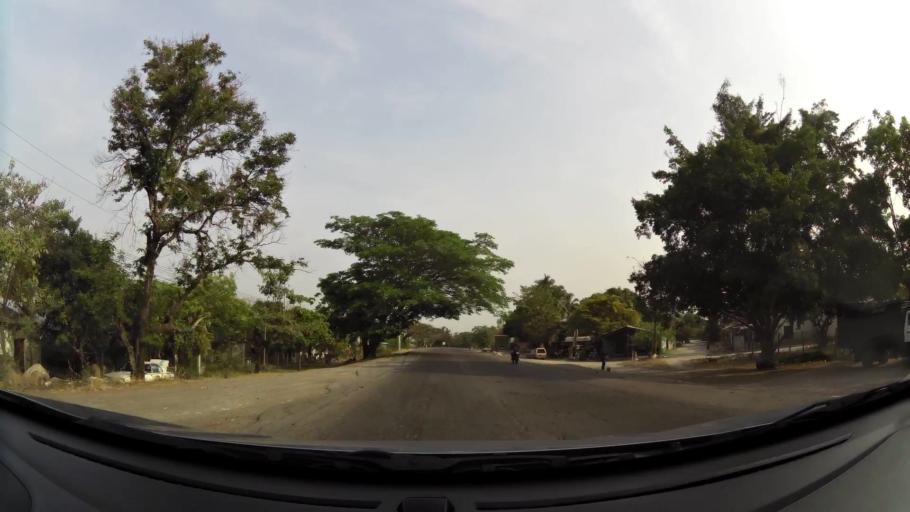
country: HN
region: Comayagua
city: Flores
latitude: 14.2890
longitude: -87.5700
